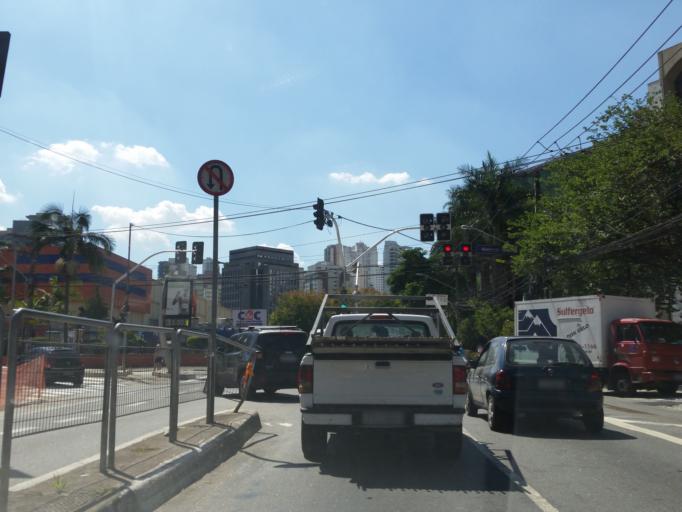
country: BR
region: Sao Paulo
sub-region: Taboao Da Serra
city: Taboao da Serra
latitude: -23.6318
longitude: -46.7367
